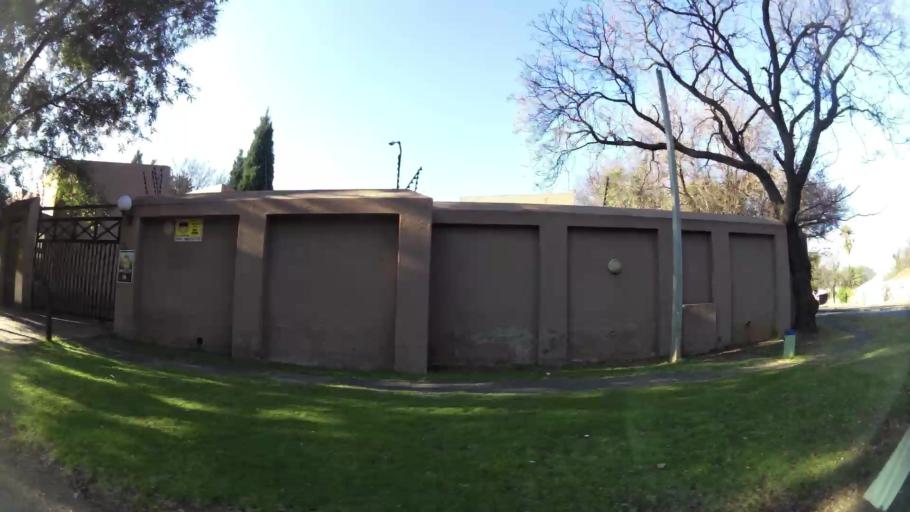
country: ZA
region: Gauteng
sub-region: City of Johannesburg Metropolitan Municipality
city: Johannesburg
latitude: -26.1379
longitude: 28.0734
